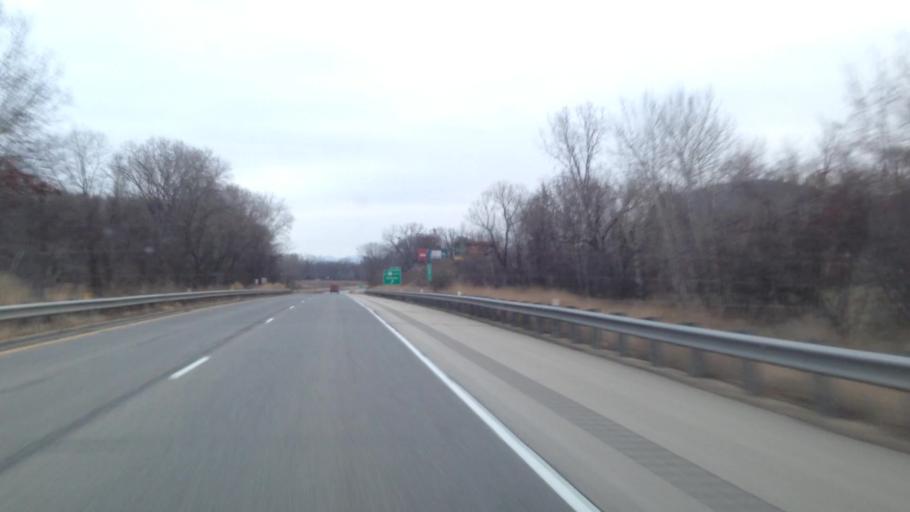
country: US
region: Wisconsin
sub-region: La Crosse County
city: Brice Prairie
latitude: 43.9167
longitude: -91.3706
